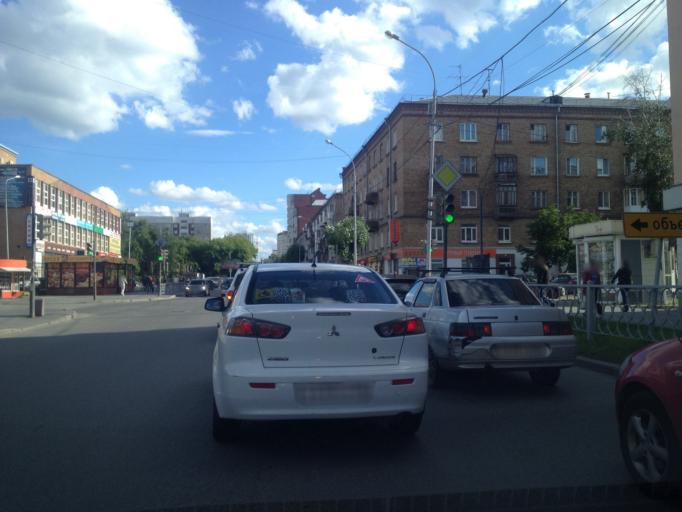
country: RU
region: Sverdlovsk
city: Yekaterinburg
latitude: 56.8337
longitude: 60.5525
